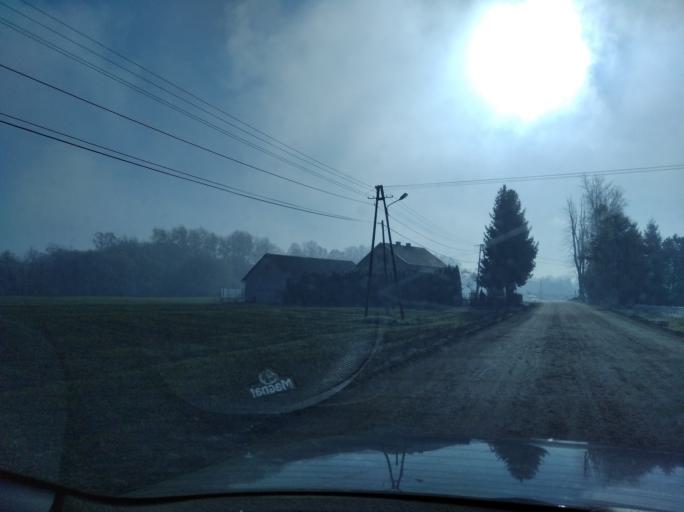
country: PL
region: Subcarpathian Voivodeship
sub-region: Powiat strzyzowski
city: Wysoka Strzyzowska
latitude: 49.8675
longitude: 21.7060
